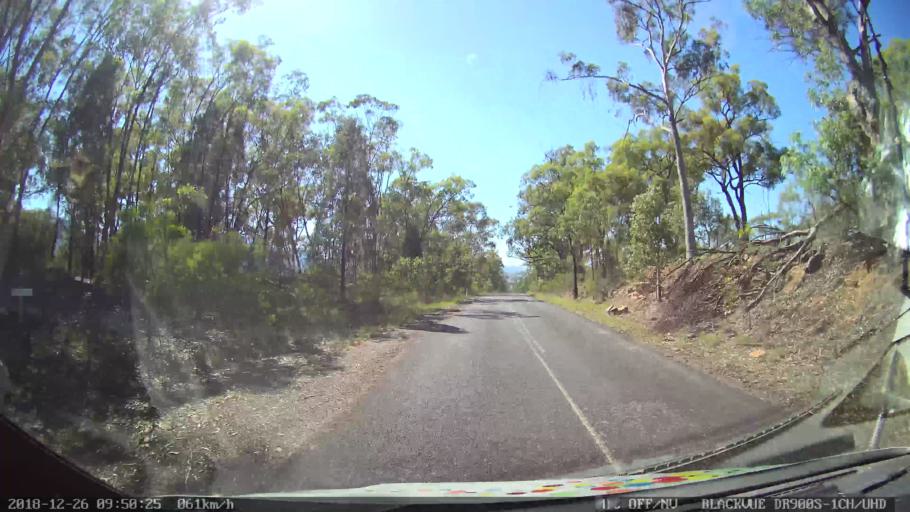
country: AU
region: New South Wales
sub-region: Mid-Western Regional
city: Kandos
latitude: -32.9970
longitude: 150.1336
